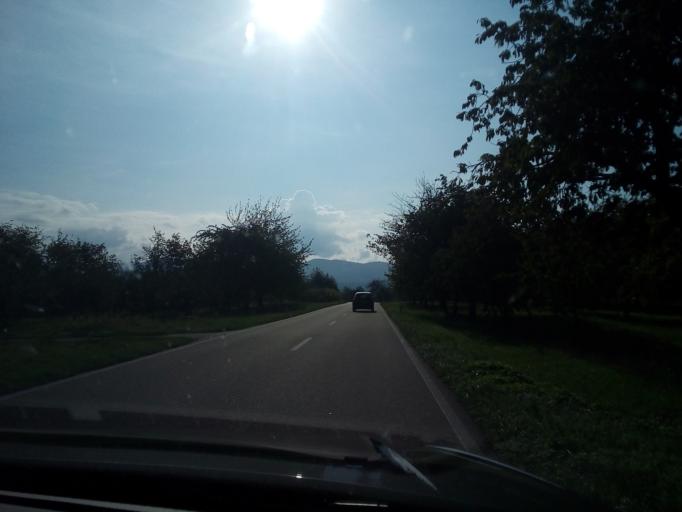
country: DE
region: Baden-Wuerttemberg
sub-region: Freiburg Region
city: Renchen
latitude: 48.5753
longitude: 8.0291
